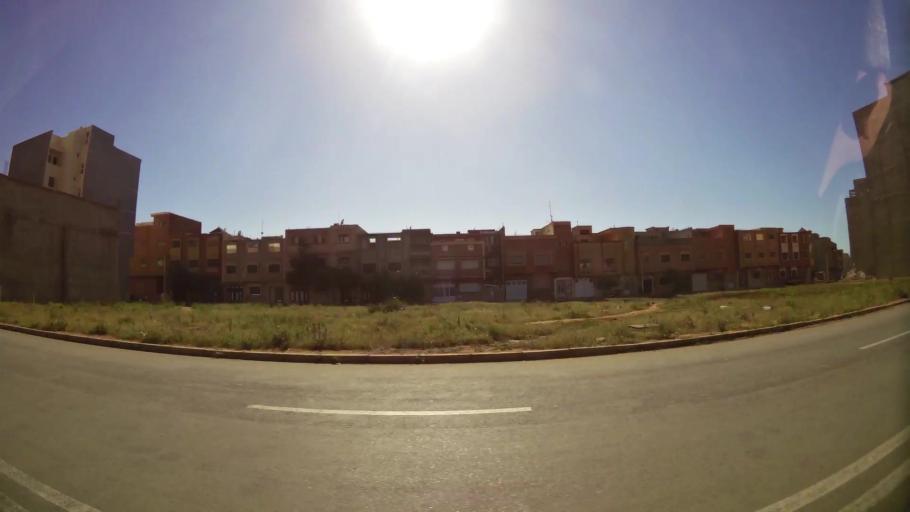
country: MA
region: Oriental
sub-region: Berkane-Taourirt
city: Berkane
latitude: 34.9395
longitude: -2.3345
